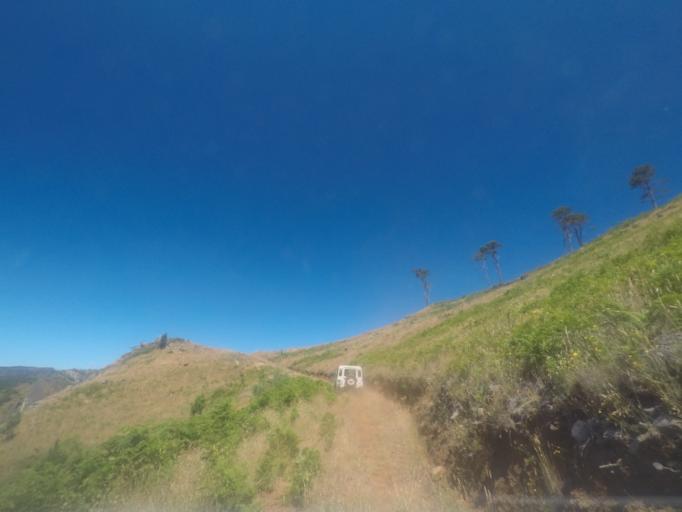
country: PT
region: Madeira
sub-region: Funchal
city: Nossa Senhora do Monte
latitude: 32.7155
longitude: -16.9131
